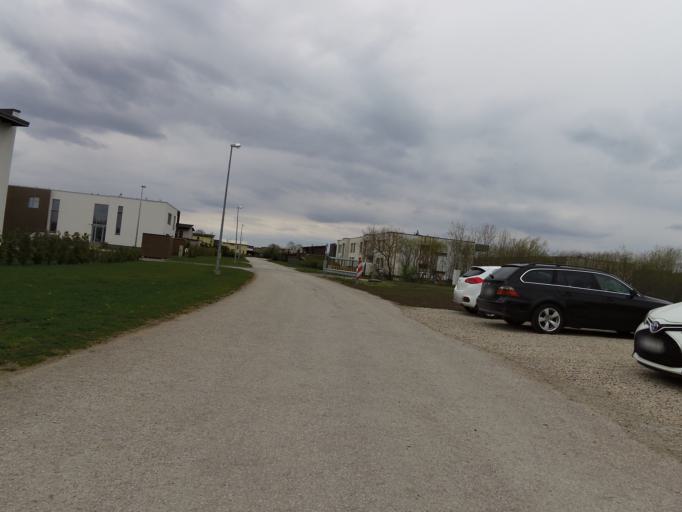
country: EE
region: Harju
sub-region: Tallinna linn
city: Tallinn
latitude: 59.3992
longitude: 24.8004
